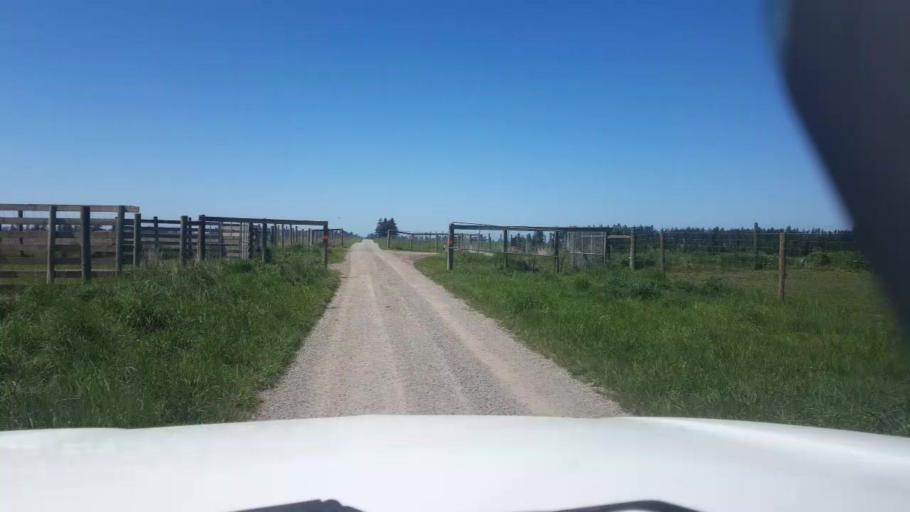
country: NZ
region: Canterbury
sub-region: Timaru District
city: Pleasant Point
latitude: -43.9407
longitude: 171.2717
